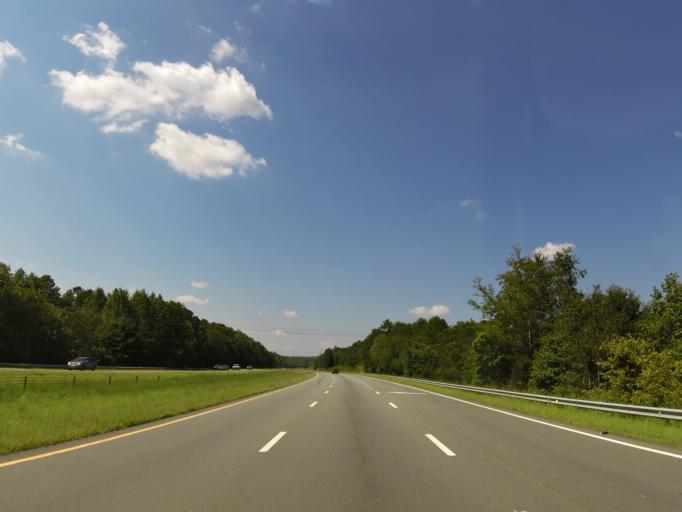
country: US
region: North Carolina
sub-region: Gaston County
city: Dallas
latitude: 35.3832
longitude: -81.2033
